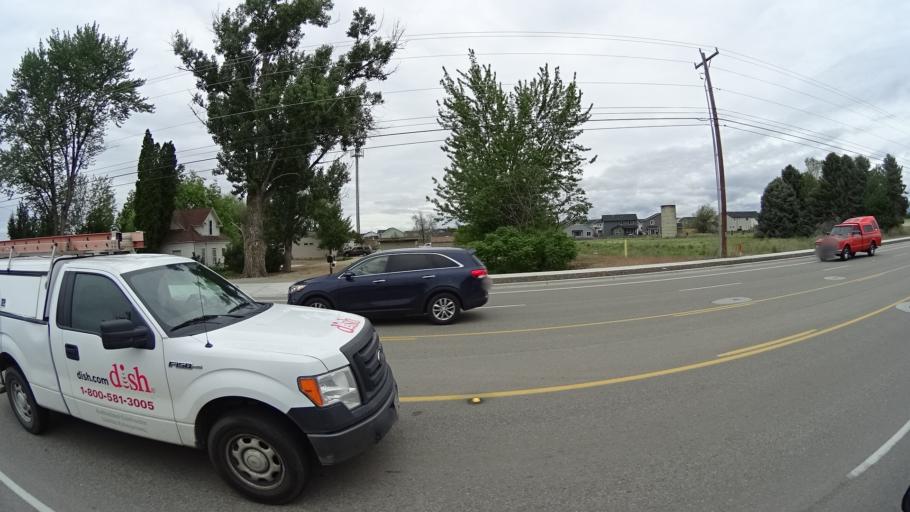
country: US
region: Idaho
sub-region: Ada County
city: Meridian
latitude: 43.6338
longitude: -116.4091
